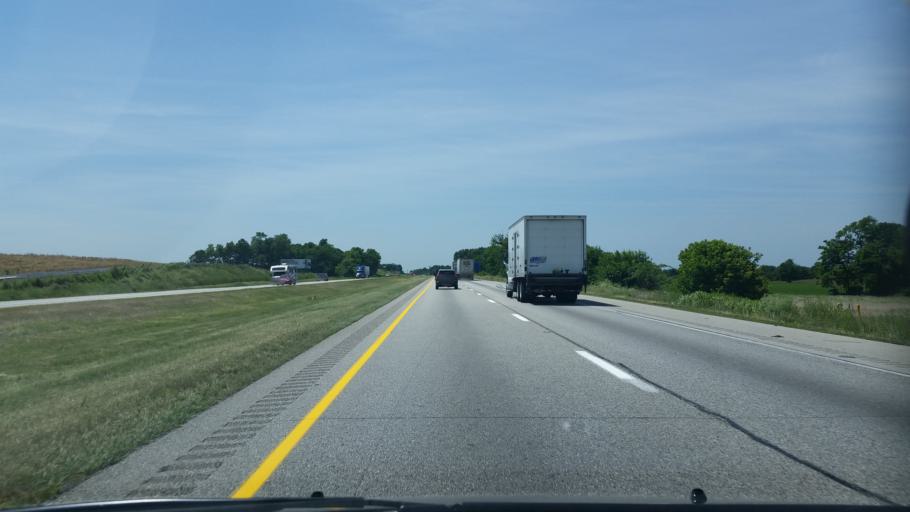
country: US
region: Pennsylvania
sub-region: Franklin County
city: Greencastle
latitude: 39.8089
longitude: -77.7056
